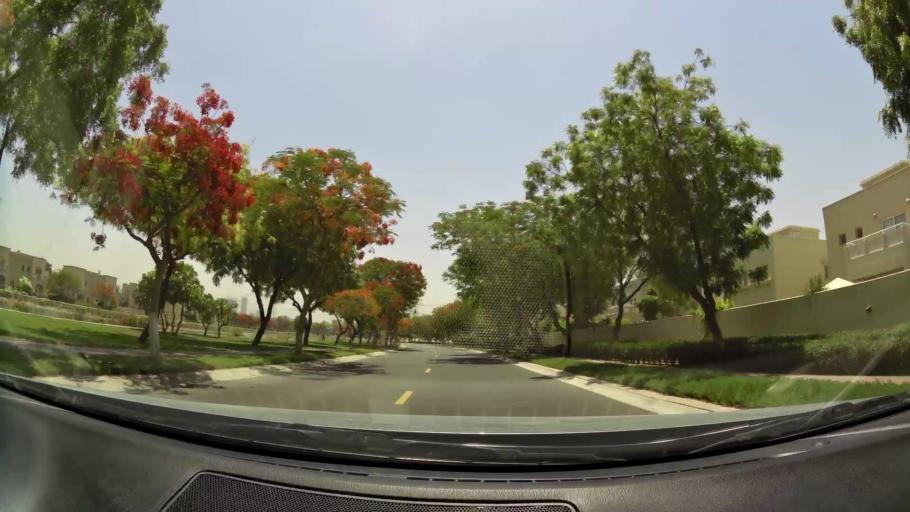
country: AE
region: Dubai
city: Dubai
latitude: 25.0483
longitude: 55.1776
